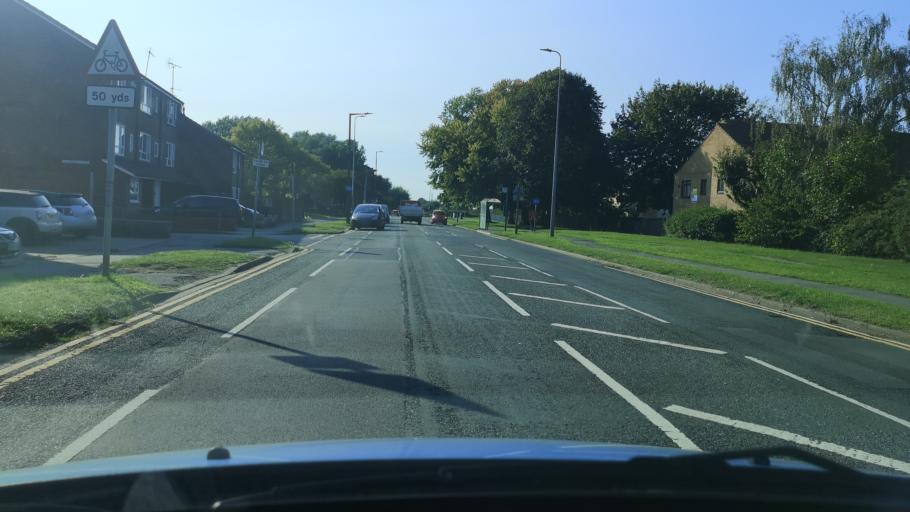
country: GB
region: England
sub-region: North Lincolnshire
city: Scunthorpe
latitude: 53.5742
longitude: -0.6798
